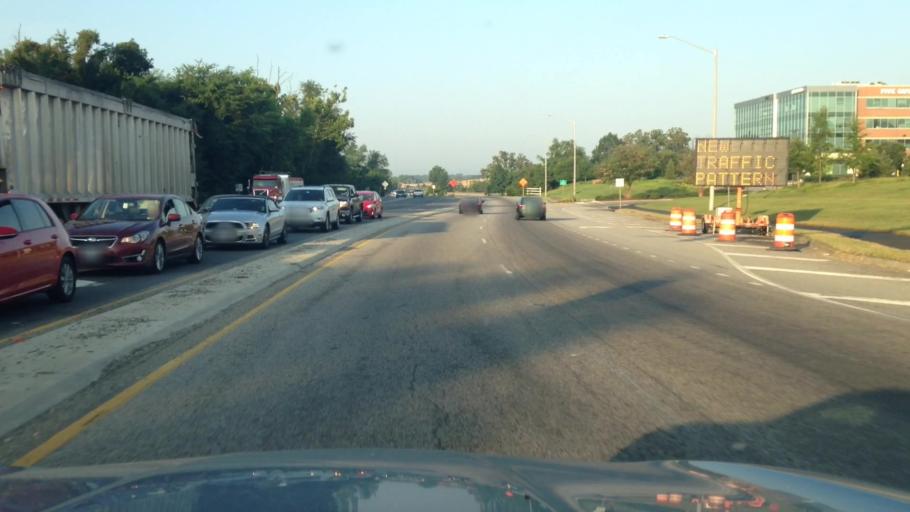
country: US
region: Virginia
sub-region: Prince William County
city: Woodbridge
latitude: 38.6702
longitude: -77.2378
